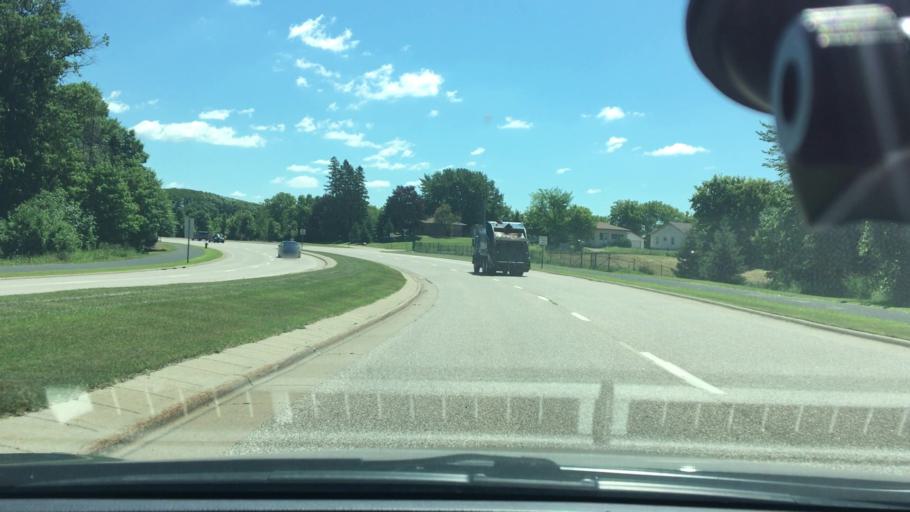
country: US
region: Minnesota
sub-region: Hennepin County
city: Maple Grove
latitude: 45.0765
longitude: -93.4687
